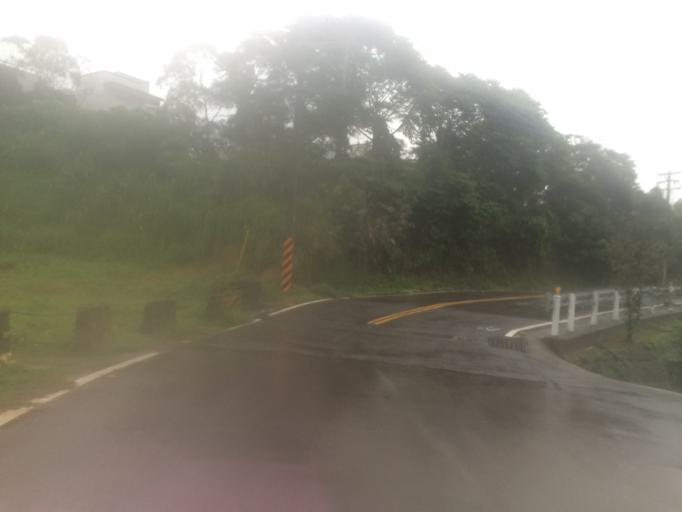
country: TW
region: Taiwan
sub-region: Hsinchu
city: Hsinchu
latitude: 24.7638
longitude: 120.9764
